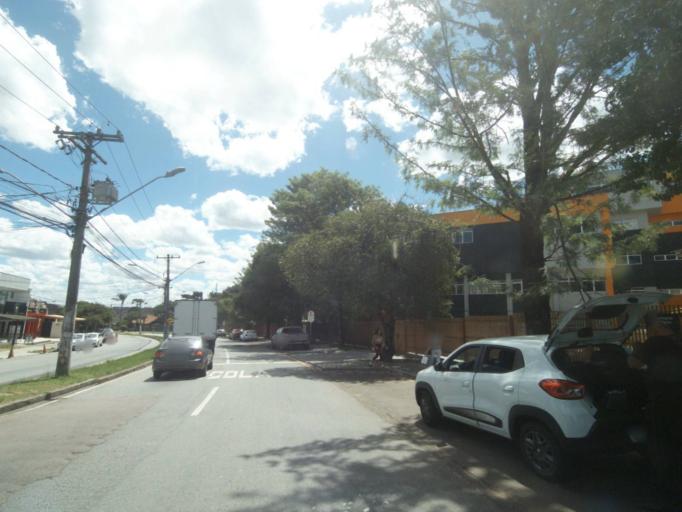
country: BR
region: Parana
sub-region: Curitiba
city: Curitiba
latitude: -25.5114
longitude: -49.3272
